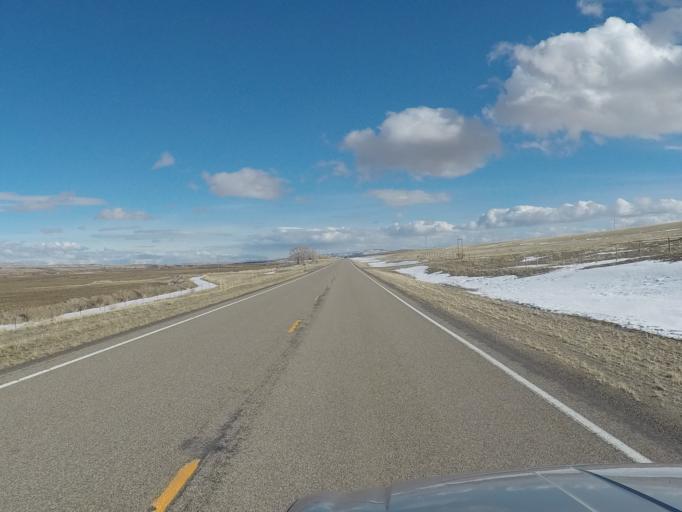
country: US
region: Montana
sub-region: Meagher County
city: White Sulphur Springs
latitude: 46.5341
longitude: -110.4310
